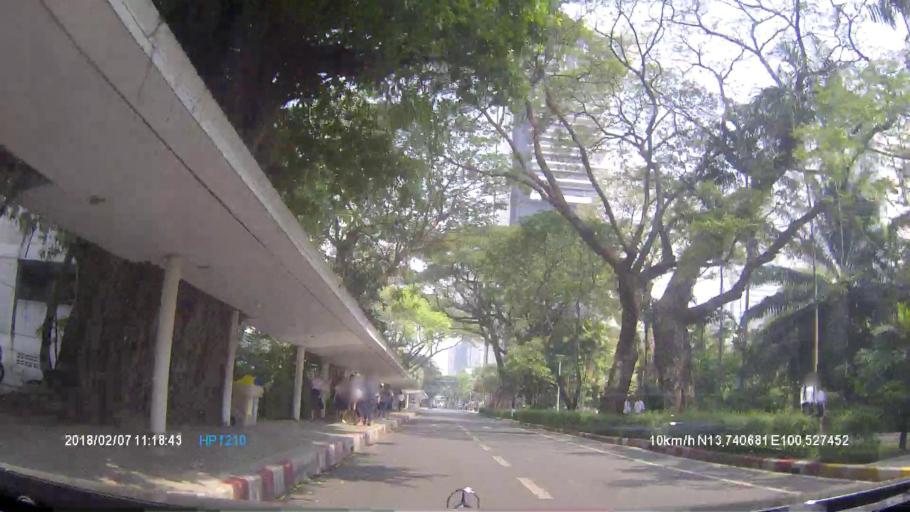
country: TH
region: Bangkok
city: Pathum Wan
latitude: 13.7408
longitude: 100.5275
